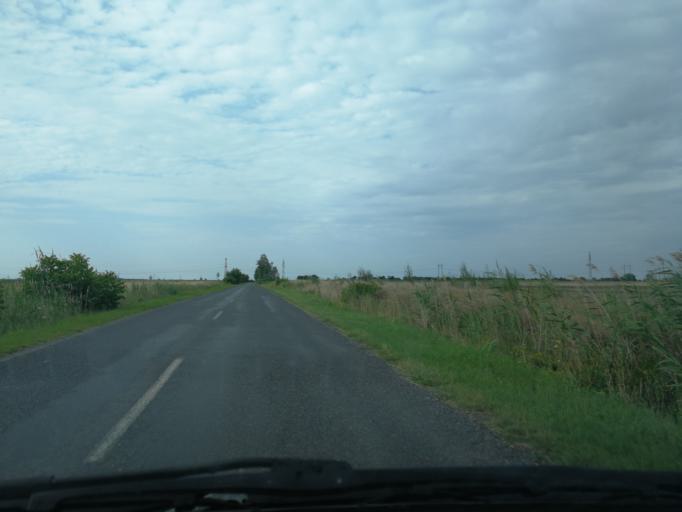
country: HU
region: Bacs-Kiskun
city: Kalocsa
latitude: 46.4820
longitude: 19.0507
